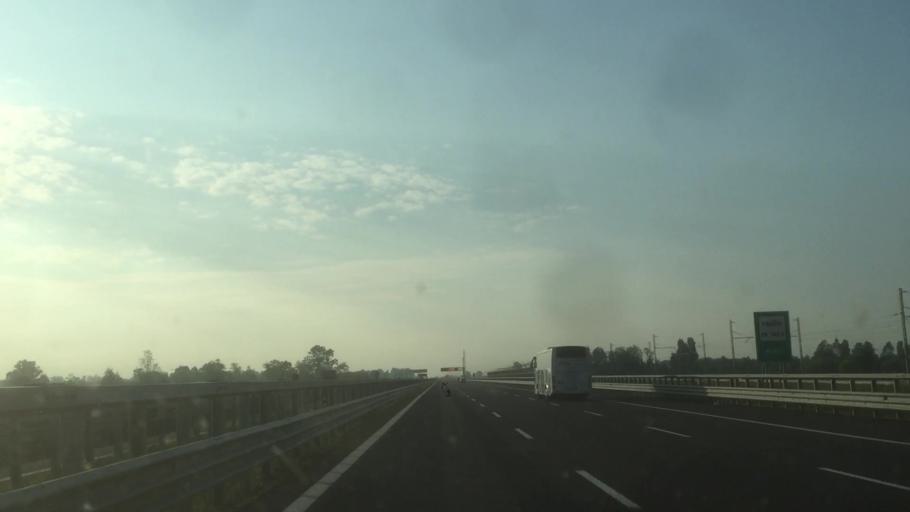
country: IT
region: Lombardy
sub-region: Provincia di Bergamo
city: Bariano
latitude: 45.5041
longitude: 9.7035
